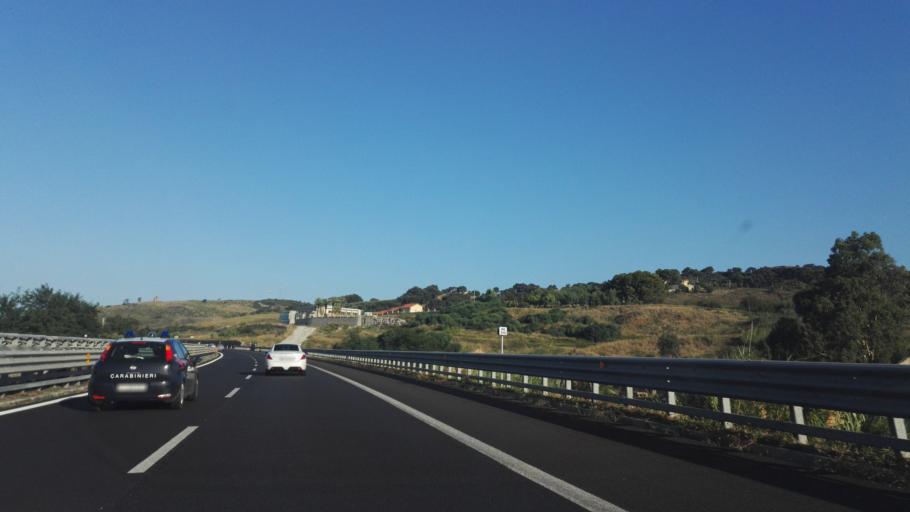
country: IT
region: Calabria
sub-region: Provincia di Catanzaro
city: Falerna Scalo
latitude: 38.9488
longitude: 16.1833
